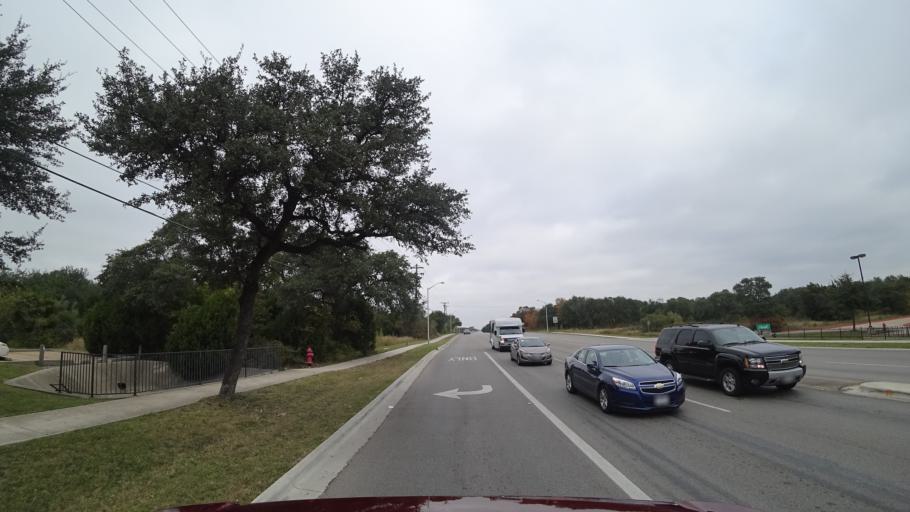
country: US
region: Texas
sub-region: Williamson County
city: Cedar Park
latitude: 30.5183
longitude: -97.8403
